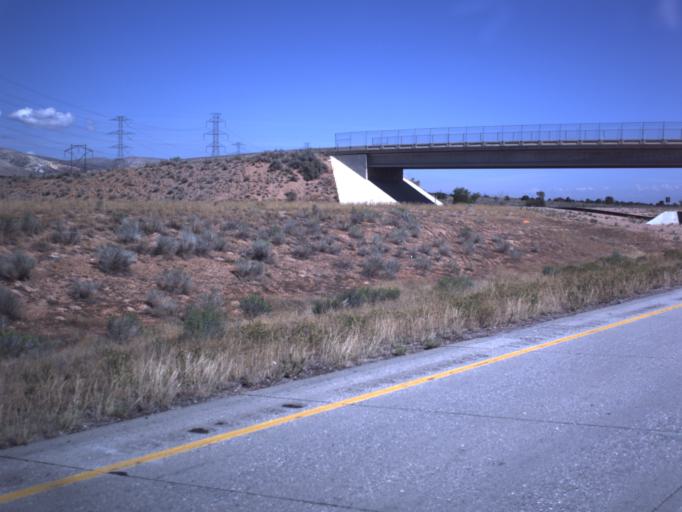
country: US
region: Utah
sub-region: Sevier County
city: Aurora
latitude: 38.8595
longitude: -111.9853
